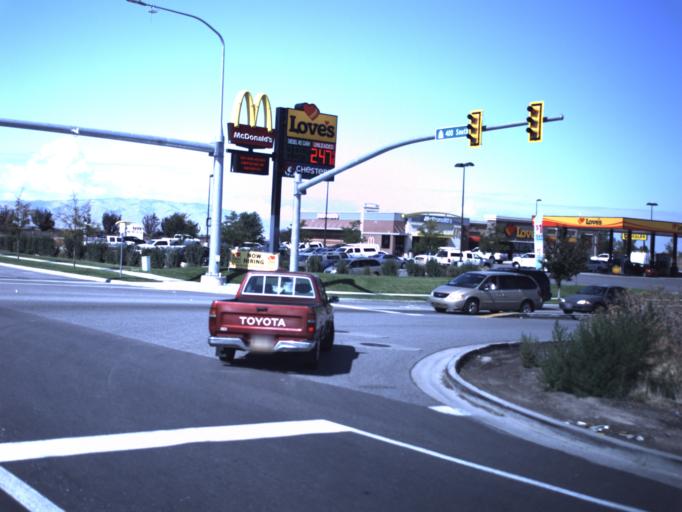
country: US
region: Utah
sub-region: Utah County
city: Springville
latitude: 40.1613
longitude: -111.6508
